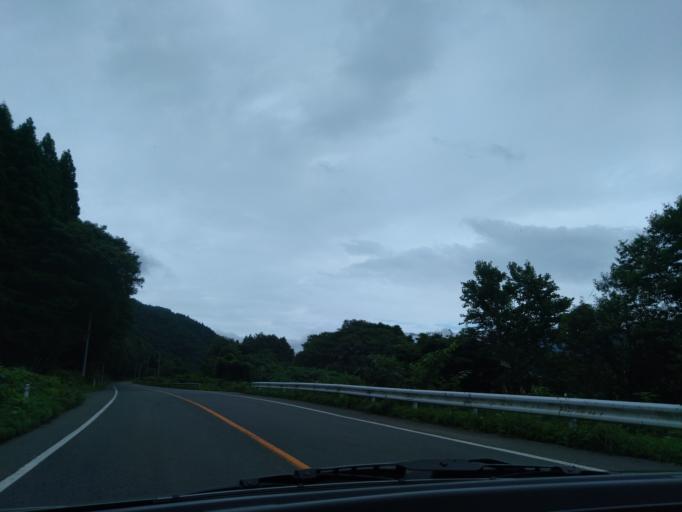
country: JP
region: Akita
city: Yokotemachi
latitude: 39.3037
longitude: 140.8164
